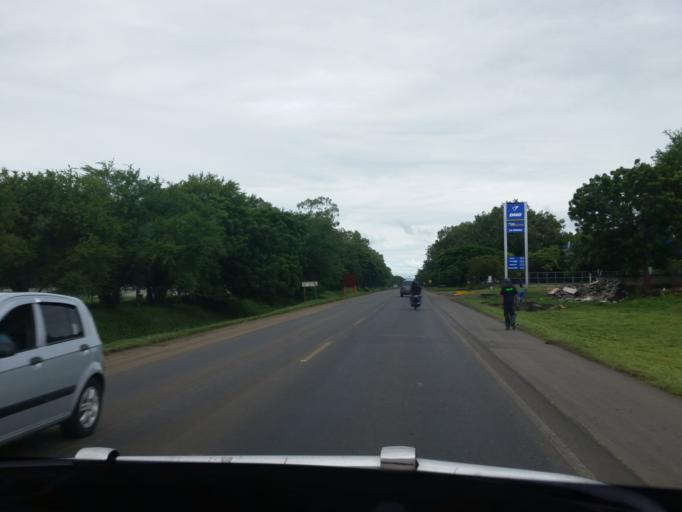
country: NI
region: Managua
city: Tipitapa
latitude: 12.2064
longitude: -86.1010
